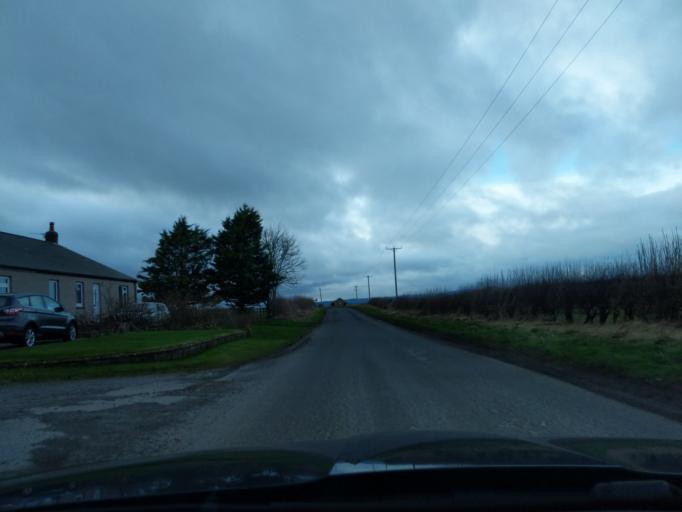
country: GB
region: England
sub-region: Northumberland
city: Ancroft
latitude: 55.7132
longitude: -2.0685
